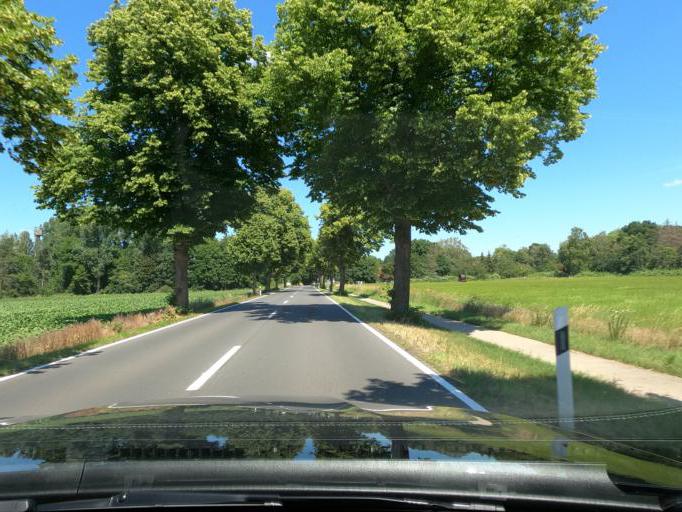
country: DE
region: Lower Saxony
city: Lehrte
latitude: 52.4131
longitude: 9.9766
